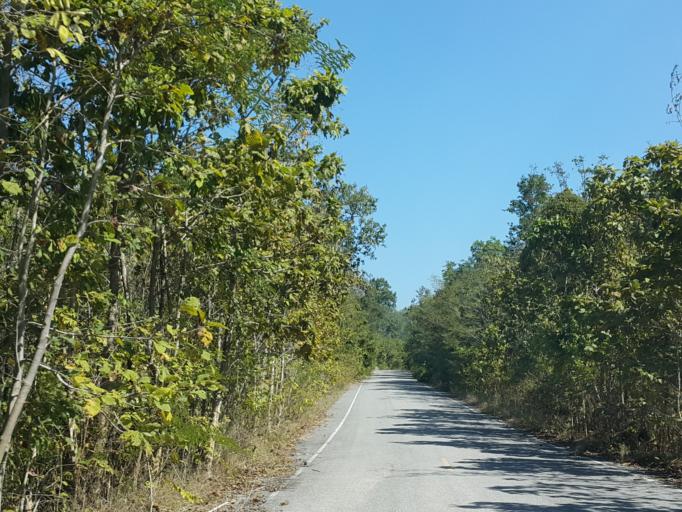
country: TH
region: Lampang
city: Thoen
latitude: 17.6450
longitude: 99.2887
